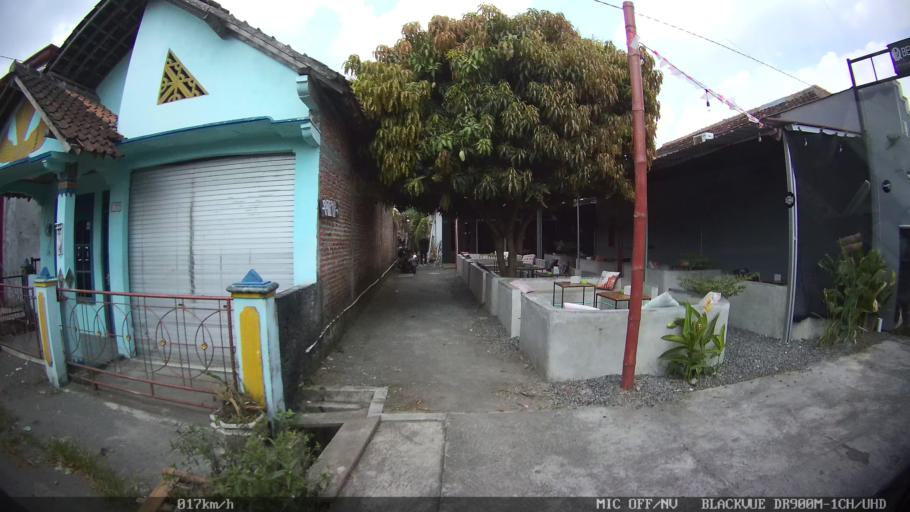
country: ID
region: Daerah Istimewa Yogyakarta
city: Yogyakarta
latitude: -7.8148
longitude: 110.4046
